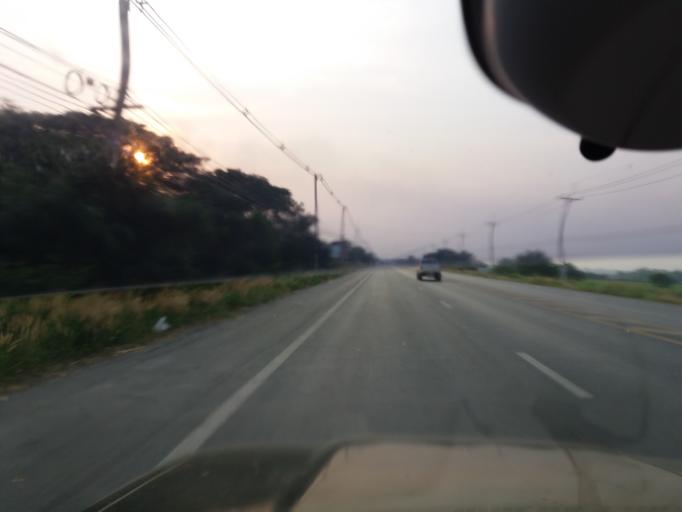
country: TH
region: Sing Buri
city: Bang Racham
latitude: 14.8828
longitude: 100.3413
